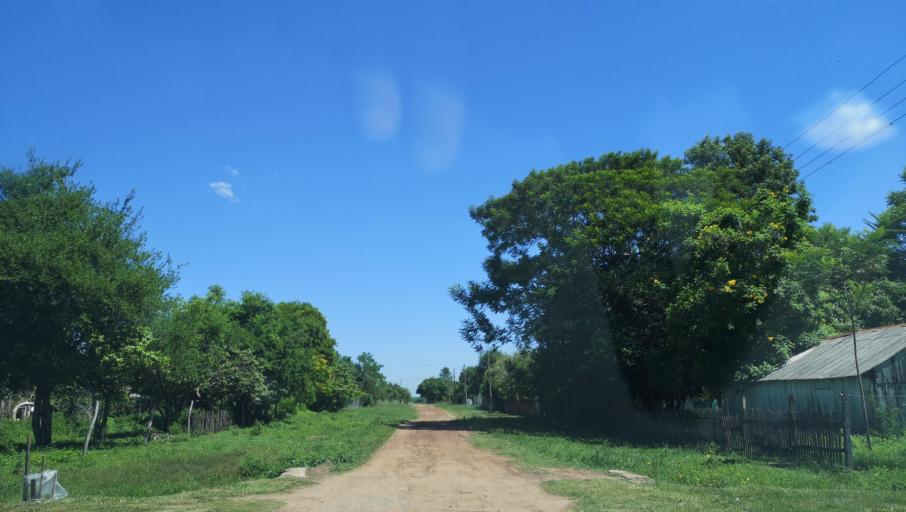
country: PY
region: Caaguazu
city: Carayao
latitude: -25.1928
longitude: -56.4002
